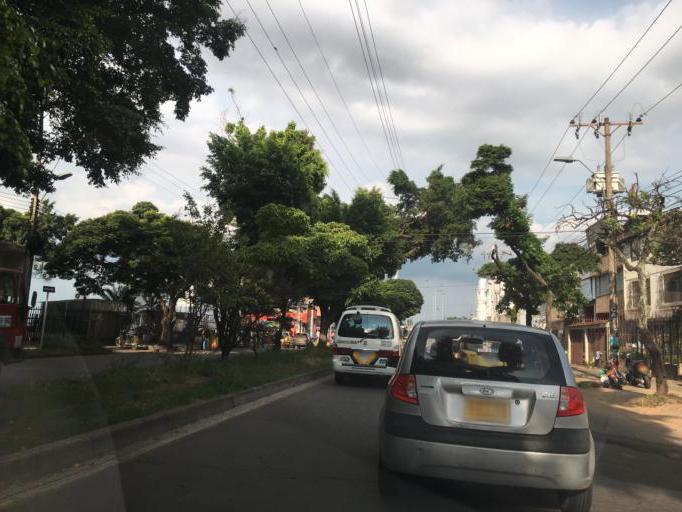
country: CO
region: Valle del Cauca
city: Cali
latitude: 3.4165
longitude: -76.5393
